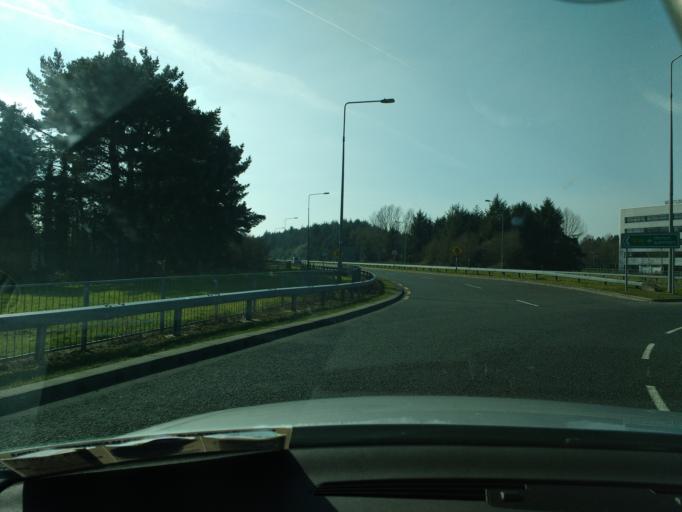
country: IE
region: Munster
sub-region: An Clar
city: Shannon
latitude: 52.7029
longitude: -8.8939
